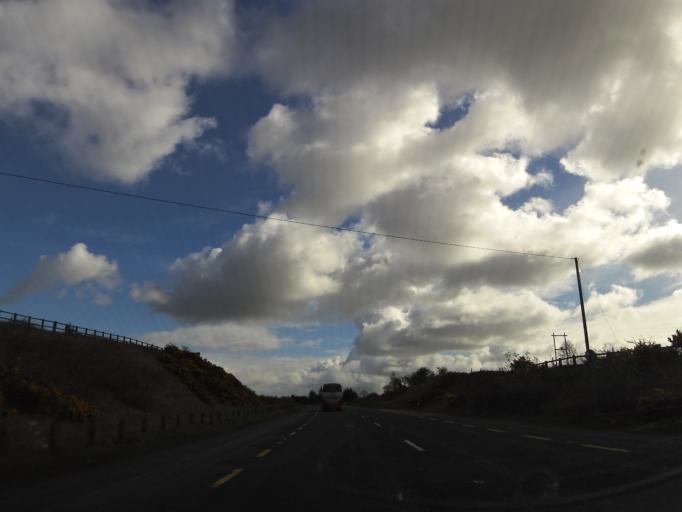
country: IE
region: Connaught
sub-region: Maigh Eo
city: Ballyhaunis
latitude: 53.8295
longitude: -8.8705
